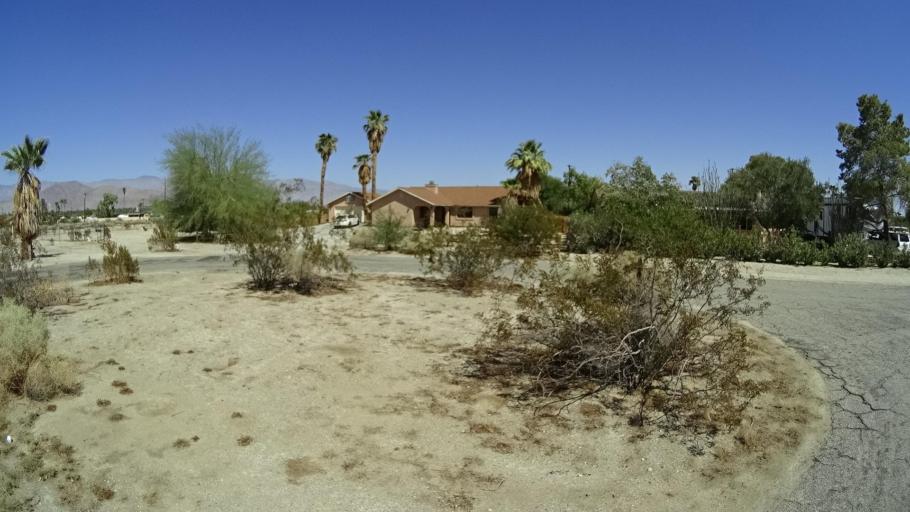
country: US
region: California
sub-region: San Diego County
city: Borrego Springs
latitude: 33.2416
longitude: -116.3725
